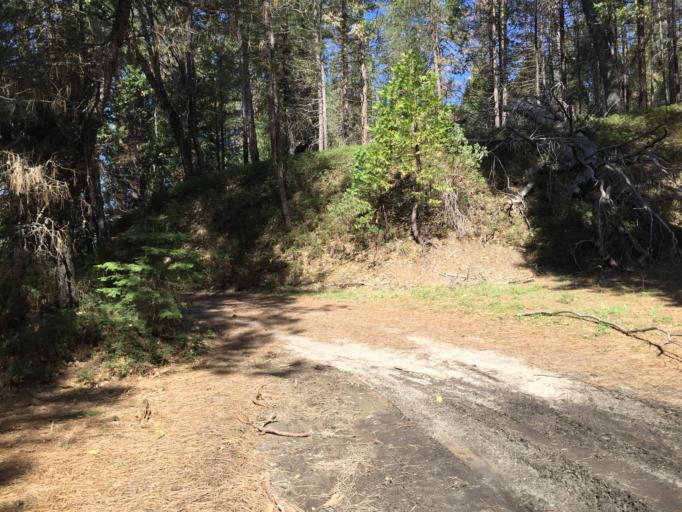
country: US
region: California
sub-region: Madera County
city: Ahwahnee
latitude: 37.5298
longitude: -119.6393
